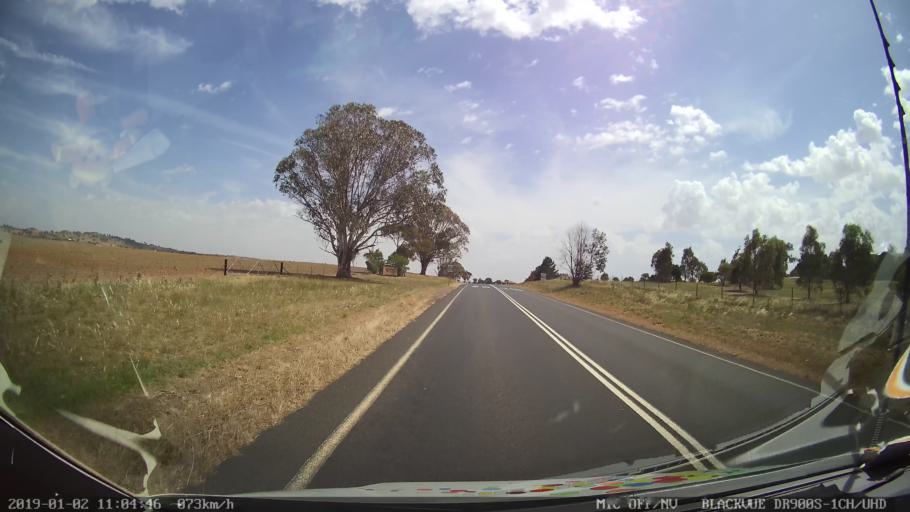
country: AU
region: New South Wales
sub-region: Young
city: Young
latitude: -34.5729
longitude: 148.3538
